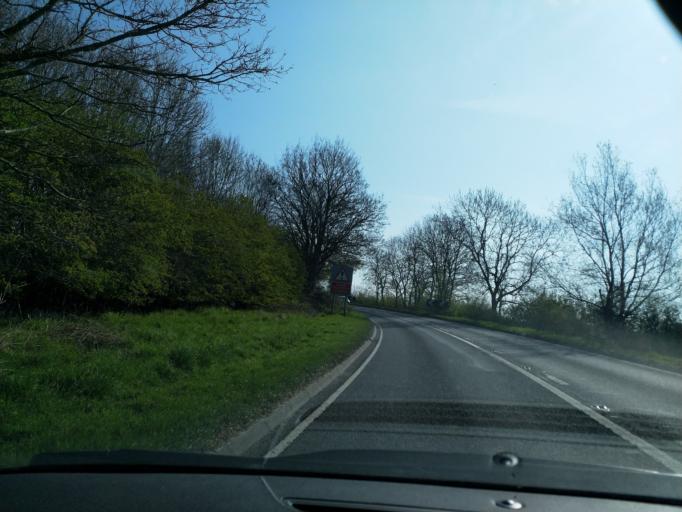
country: GB
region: England
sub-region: Warwickshire
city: Stratford-upon-Avon
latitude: 52.1780
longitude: -1.7797
